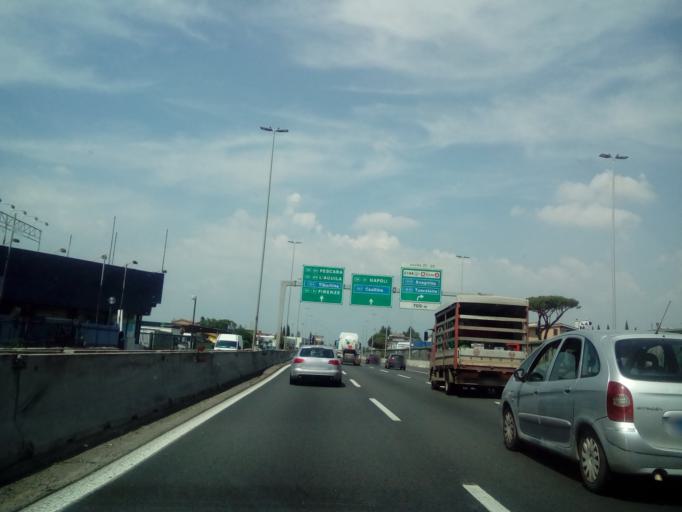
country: IT
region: Latium
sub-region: Citta metropolitana di Roma Capitale
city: Ciampino
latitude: 41.8278
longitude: 12.5839
